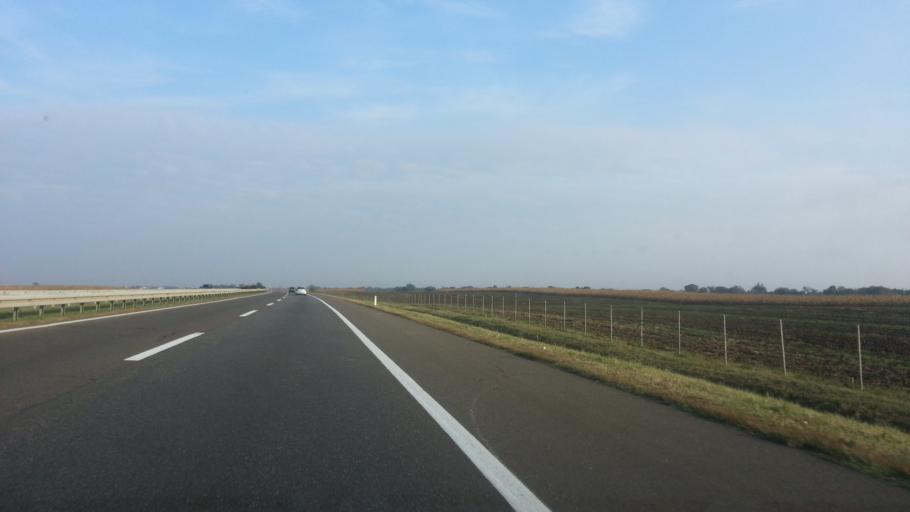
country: RS
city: Novi Banovci
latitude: 44.9265
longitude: 20.3018
